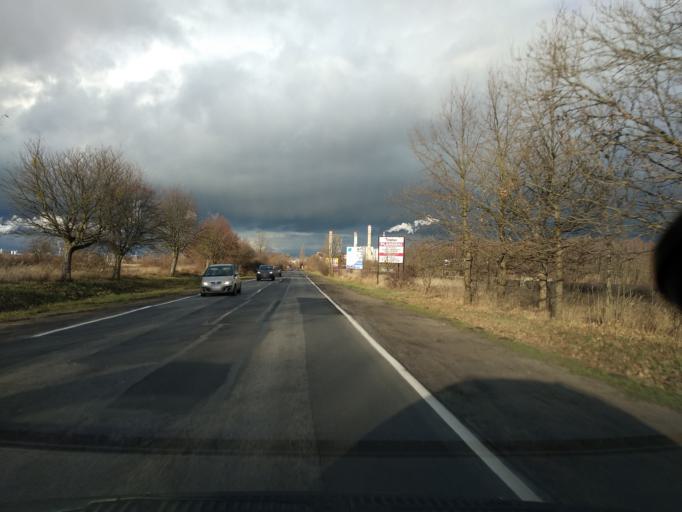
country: PL
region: Greater Poland Voivodeship
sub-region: Konin
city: Konin
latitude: 52.2711
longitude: 18.2670
